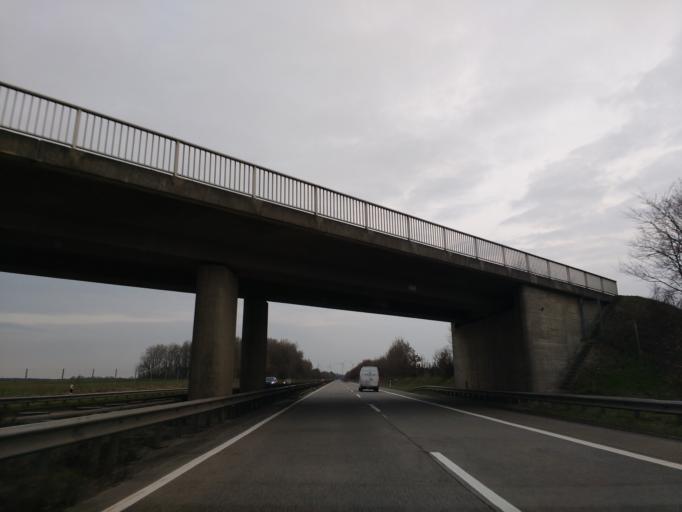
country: DE
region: Lower Saxony
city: Langen
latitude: 53.6467
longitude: 8.6624
